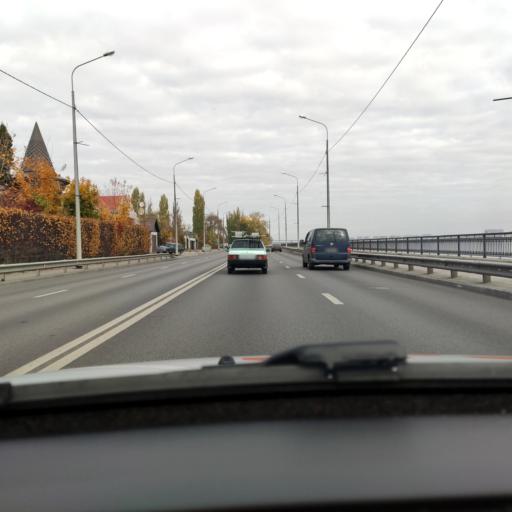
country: RU
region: Voronezj
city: Voronezh
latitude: 51.6759
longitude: 39.2262
